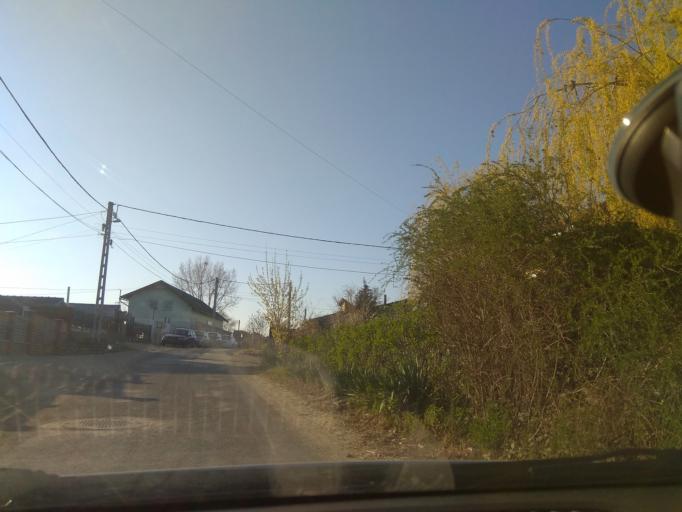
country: HU
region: Pest
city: Szigethalom
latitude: 47.3204
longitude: 19.0265
